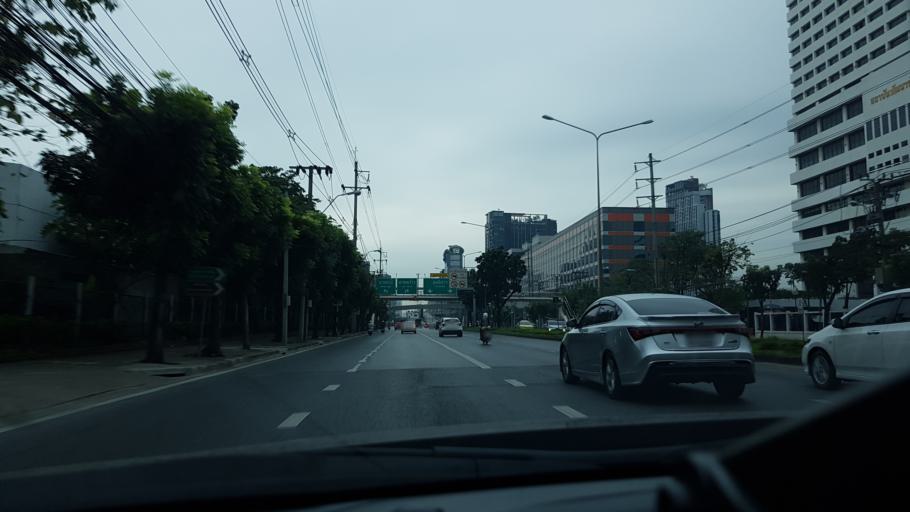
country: TH
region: Bangkok
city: Chatuchak
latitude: 13.8114
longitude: 100.5754
